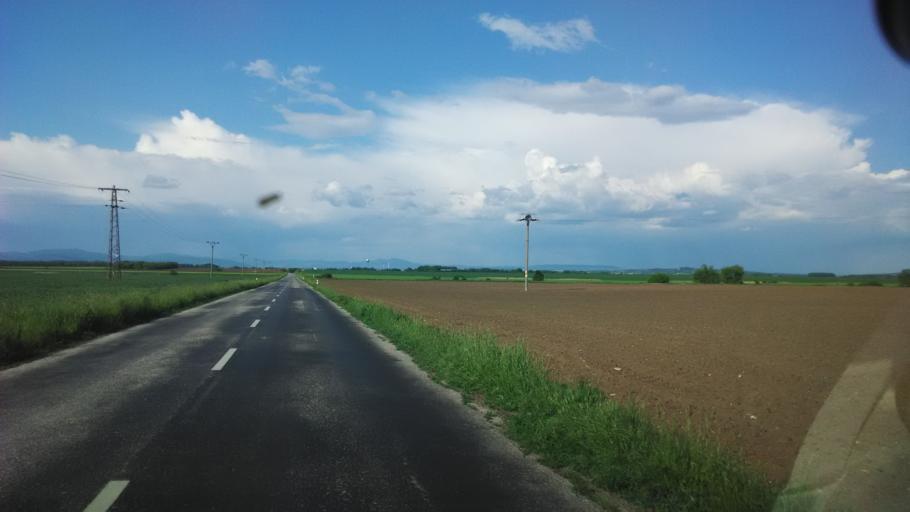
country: SK
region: Nitriansky
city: Levice
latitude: 48.1430
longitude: 18.5277
